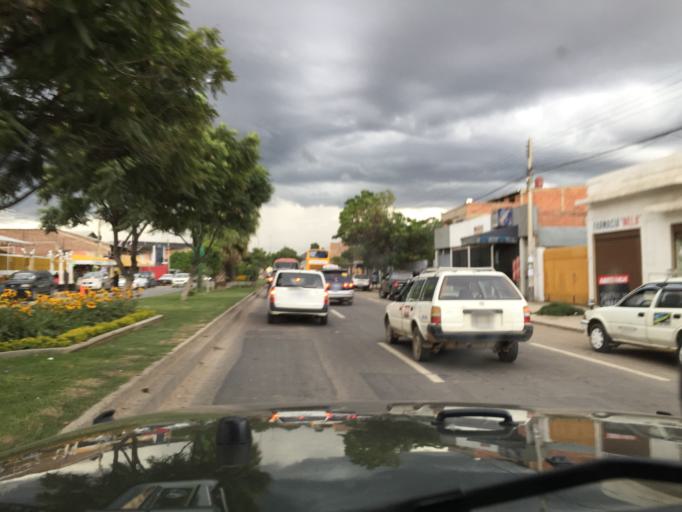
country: BO
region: Cochabamba
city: Cochabamba
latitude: -17.4055
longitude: -66.1783
